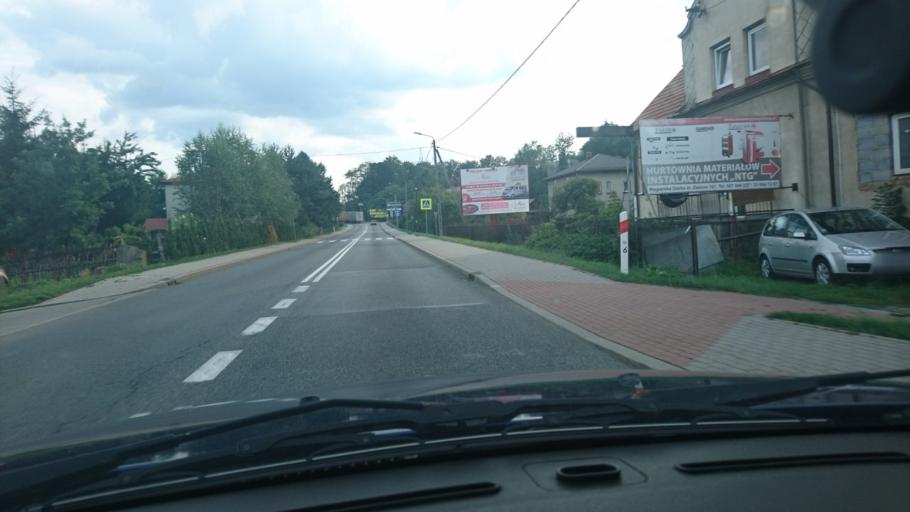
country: PL
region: Silesian Voivodeship
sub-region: Powiat zywiecki
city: Wegierska Gorka
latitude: 49.6115
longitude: 19.1180
